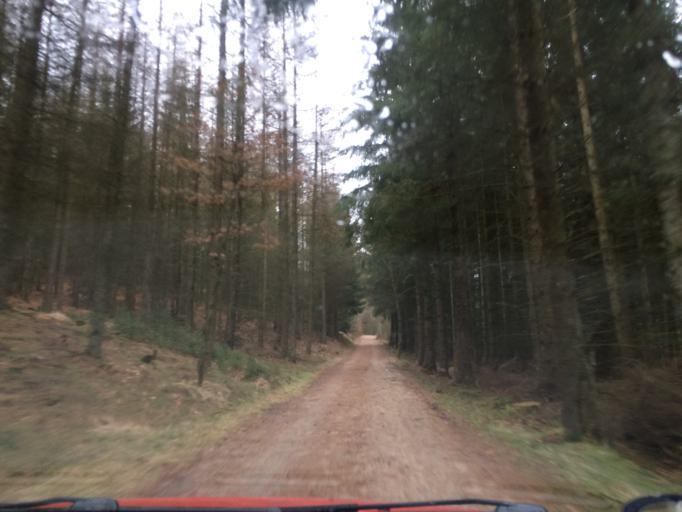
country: DK
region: Central Jutland
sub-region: Silkeborg Kommune
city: Virklund
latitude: 56.0337
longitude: 9.4755
